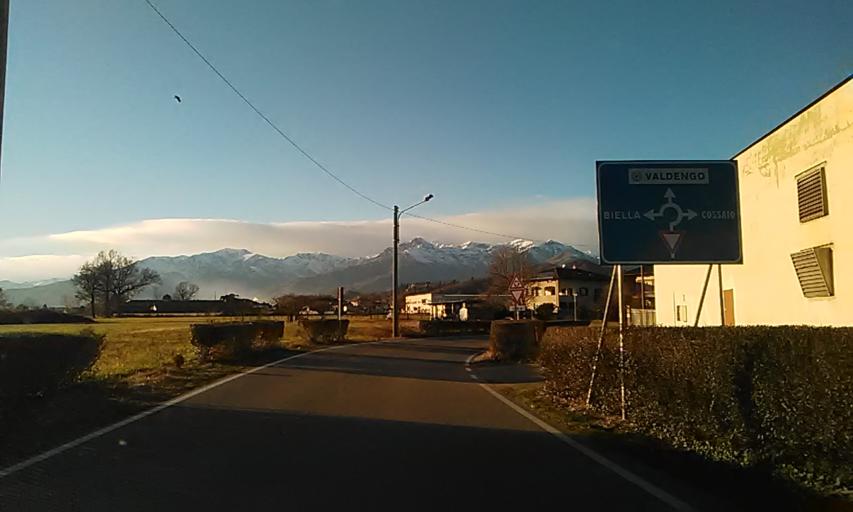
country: IT
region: Piedmont
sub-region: Provincia di Biella
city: Valdengo
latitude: 45.5619
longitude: 8.1399
